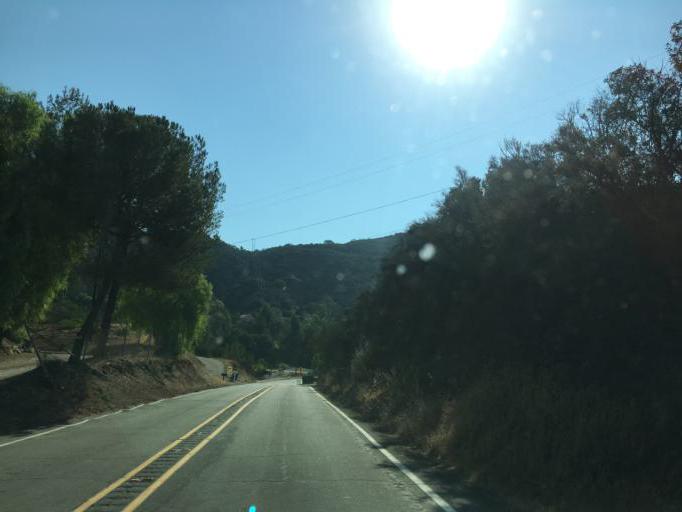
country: US
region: California
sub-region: Los Angeles County
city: Topanga
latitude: 34.1014
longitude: -118.6572
